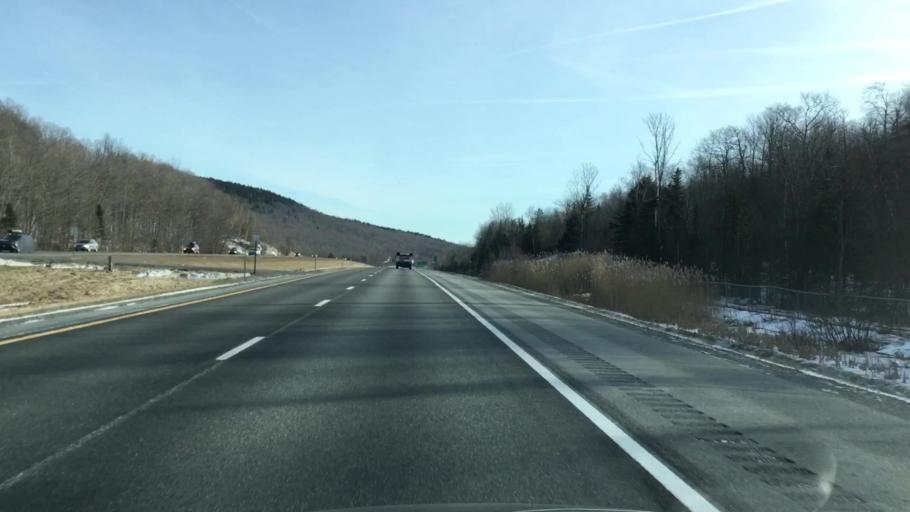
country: US
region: New Hampshire
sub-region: Grafton County
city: Enfield
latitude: 43.5722
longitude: -72.1575
